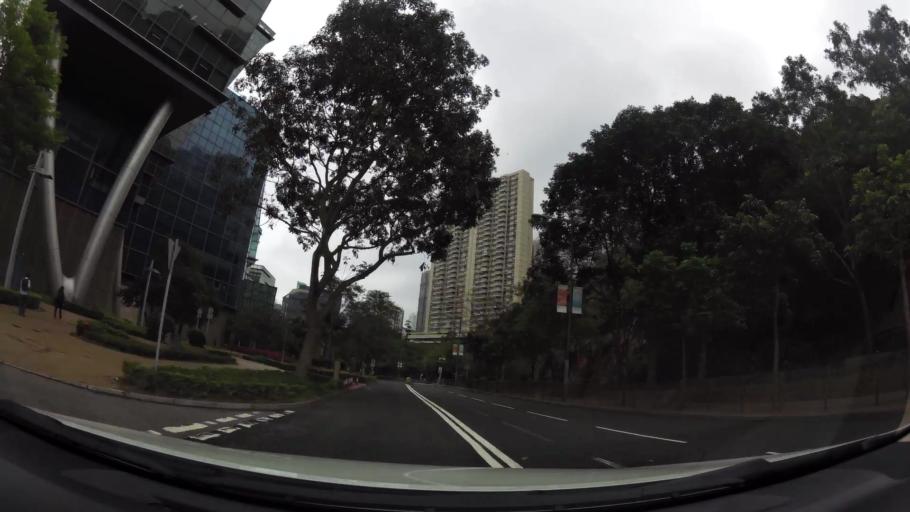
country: HK
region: Central and Western
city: Central
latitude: 22.2588
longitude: 114.1327
